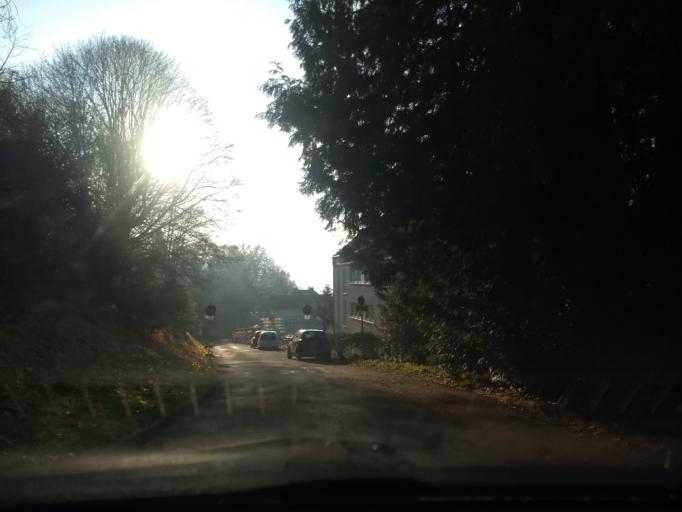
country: DE
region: Baden-Wuerttemberg
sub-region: Karlsruhe Region
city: Baden-Baden
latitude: 48.7594
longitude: 8.2513
